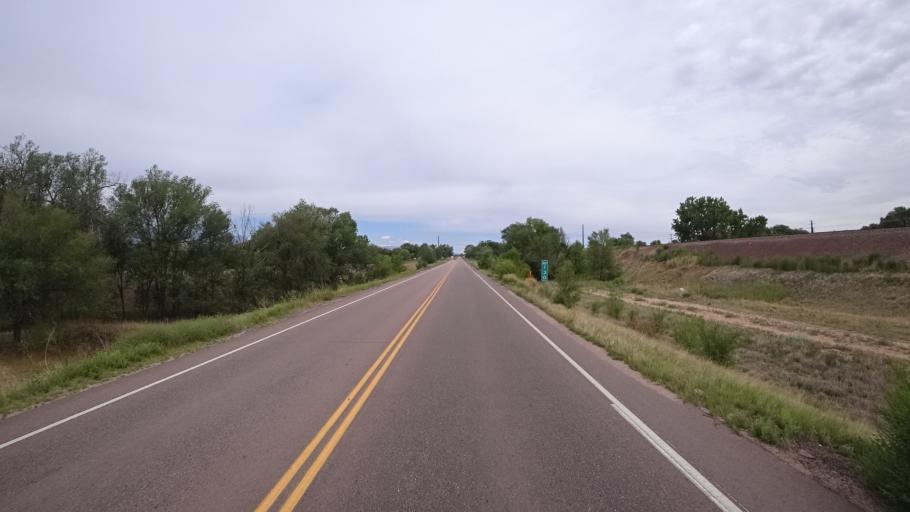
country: US
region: Colorado
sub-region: El Paso County
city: Fountain
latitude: 38.7017
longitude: -104.7082
